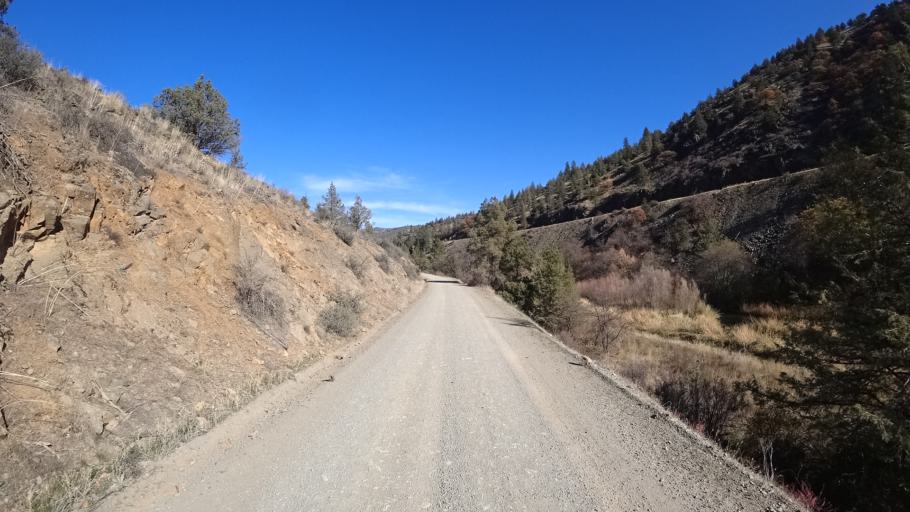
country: US
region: California
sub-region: Siskiyou County
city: Yreka
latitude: 41.7952
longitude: -122.6071
